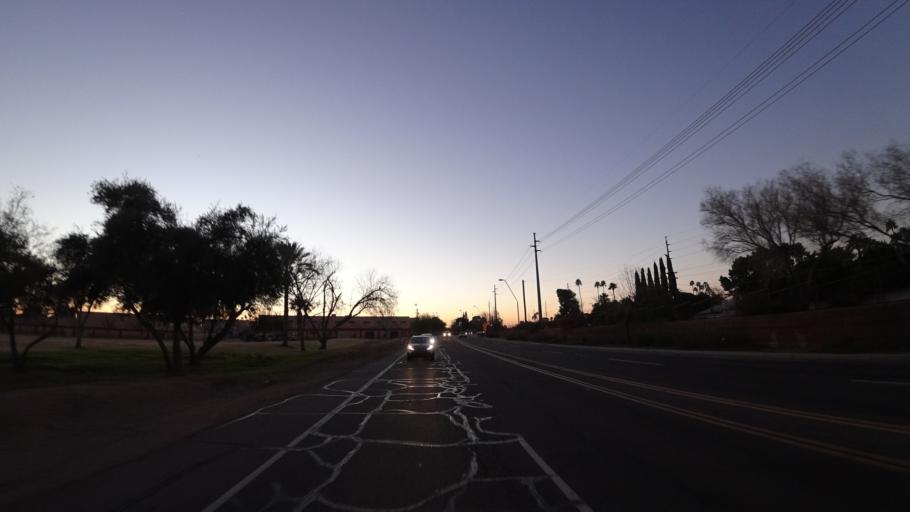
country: US
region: Arizona
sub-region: Maricopa County
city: Paradise Valley
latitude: 33.4890
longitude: -111.9622
